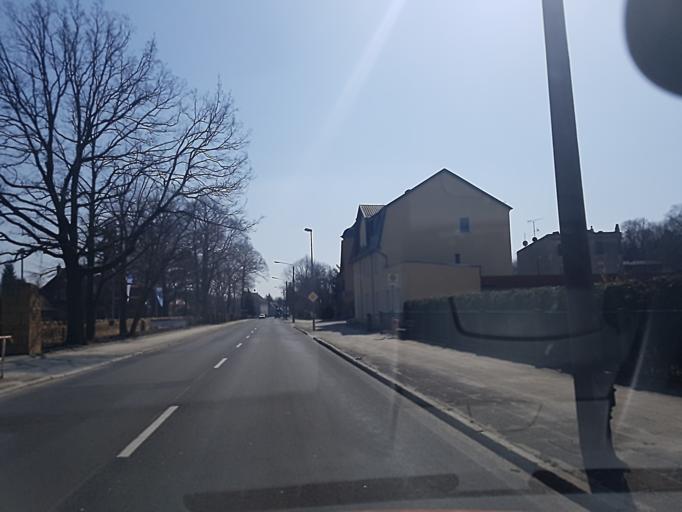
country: DE
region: Brandenburg
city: Tschernitz
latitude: 51.6231
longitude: 14.5892
